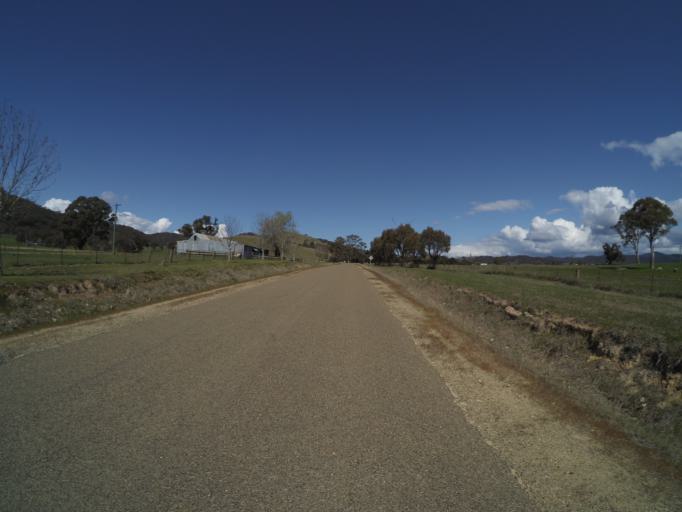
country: AU
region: Australian Capital Territory
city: Macquarie
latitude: -35.1482
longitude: 148.8829
